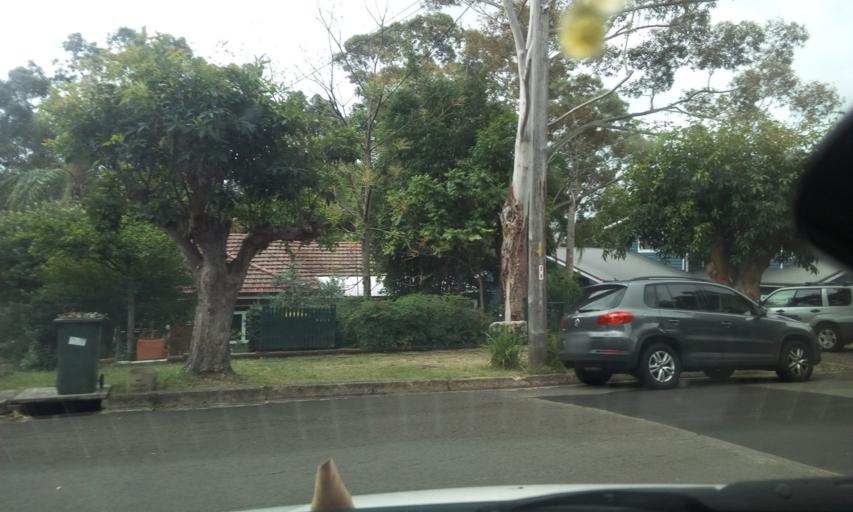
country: AU
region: New South Wales
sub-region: Wollongong
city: Keiraville
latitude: -34.4151
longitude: 150.8692
